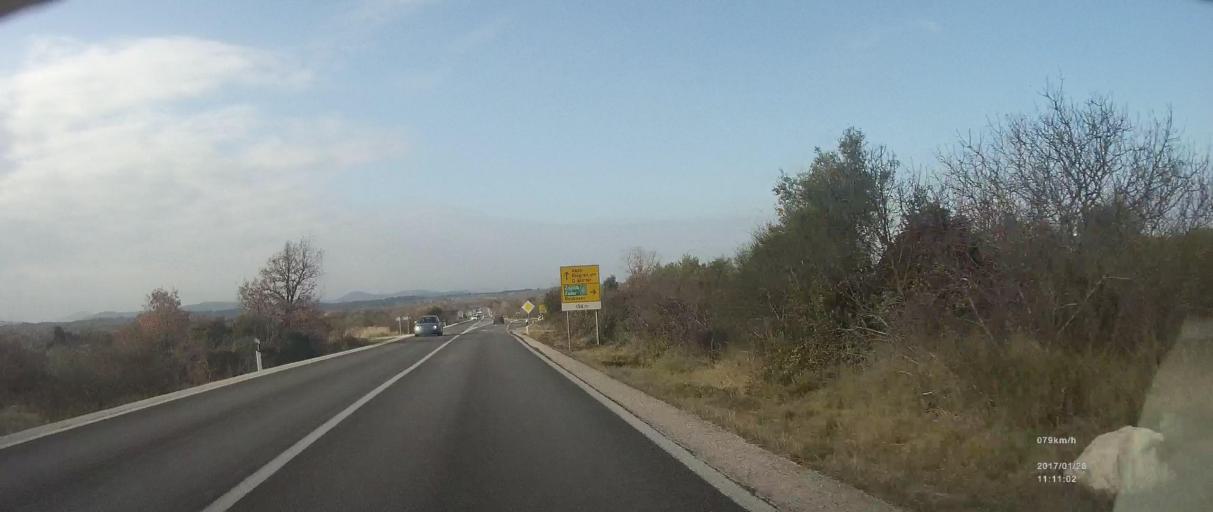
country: HR
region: Sibensko-Kniniska
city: Zaton
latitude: 43.7614
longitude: 15.8407
